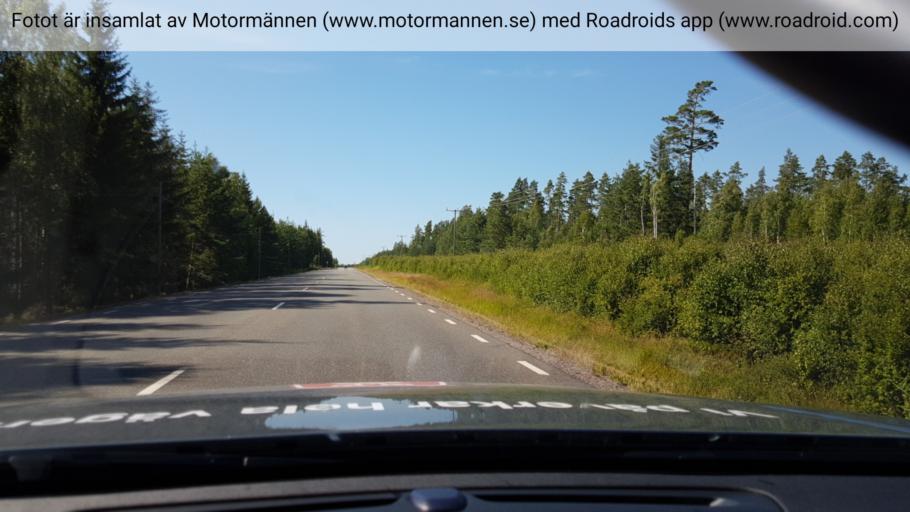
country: SE
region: Vaestra Goetaland
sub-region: Karlsborgs Kommun
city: Molltorp
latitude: 58.5884
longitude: 14.4155
